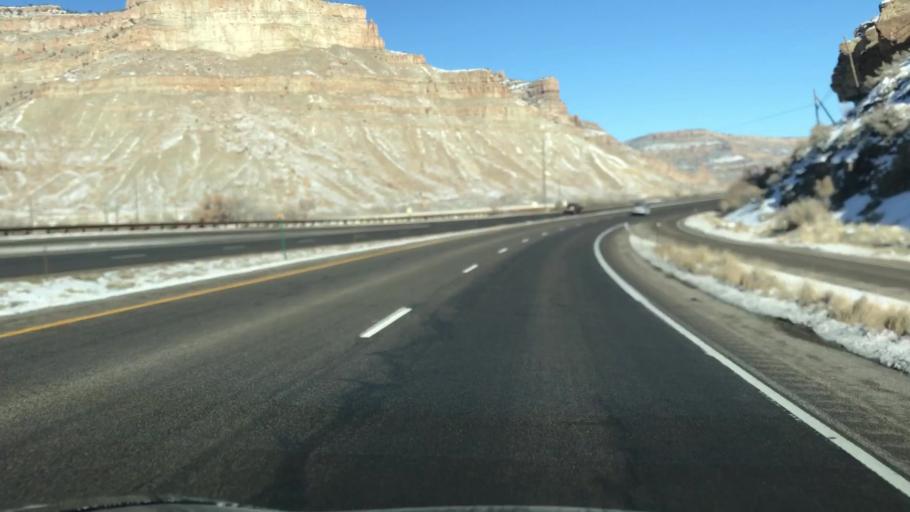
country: US
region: Colorado
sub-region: Mesa County
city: Palisade
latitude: 39.1454
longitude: -108.3155
